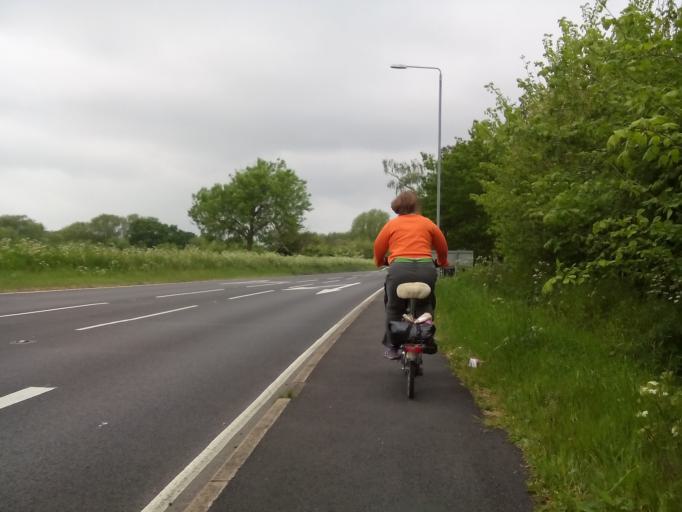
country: GB
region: England
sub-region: Cambridgeshire
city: Hemingford Grey
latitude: 52.3362
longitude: -0.1319
